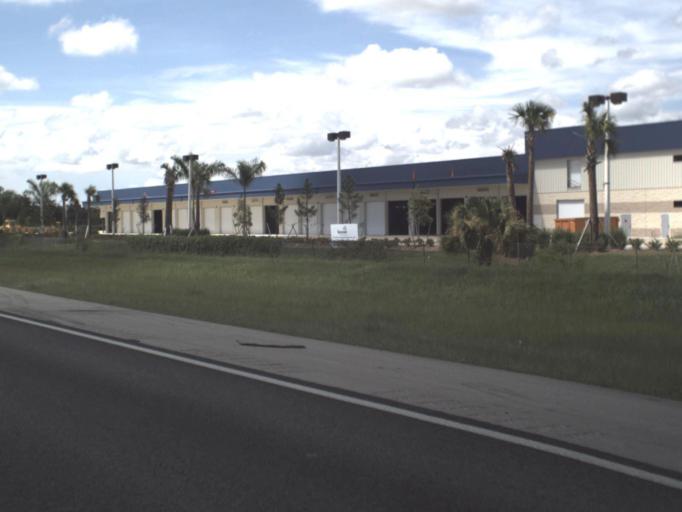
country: US
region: Florida
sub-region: Lee County
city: Tice
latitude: 26.6765
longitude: -81.7991
